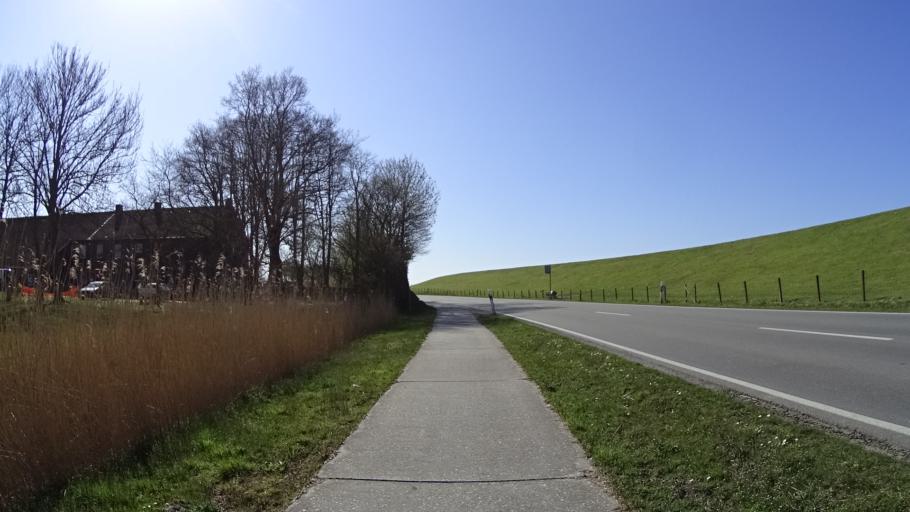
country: DE
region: Lower Saxony
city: Jemgum
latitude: 53.2496
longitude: 7.4056
